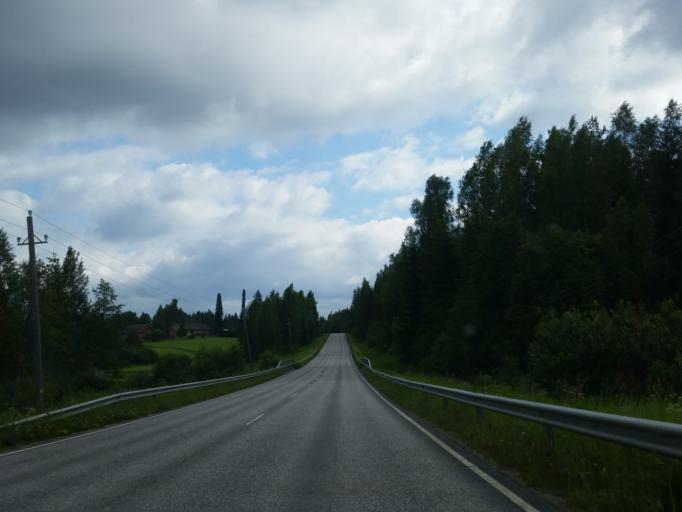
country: FI
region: Northern Savo
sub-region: Kuopio
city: Kuopio
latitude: 62.8463
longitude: 27.5251
